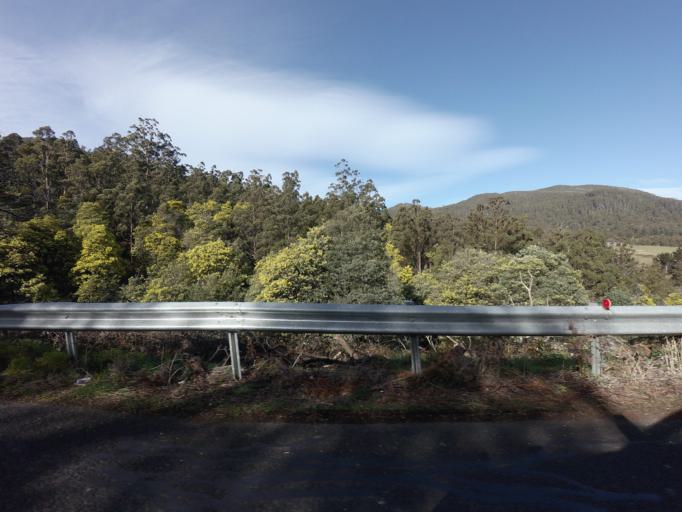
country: AU
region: Tasmania
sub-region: Kingborough
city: Kettering
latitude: -43.1729
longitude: 147.1665
